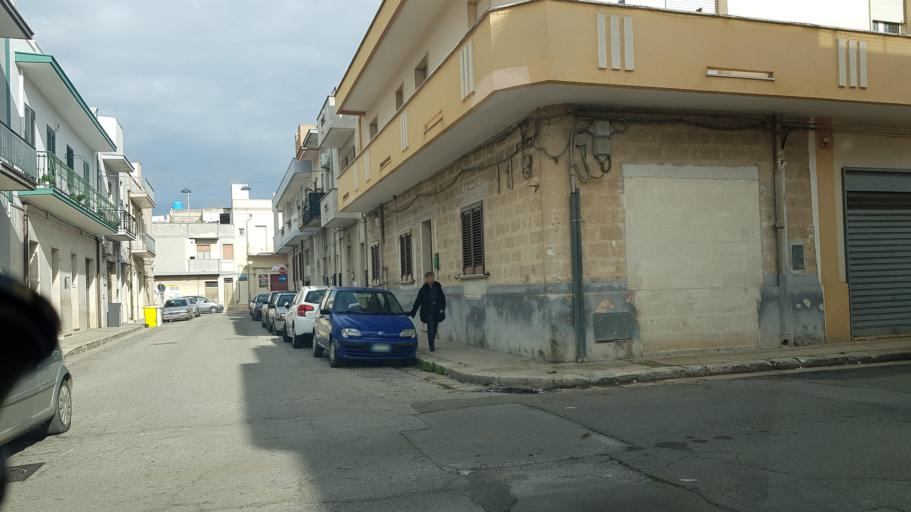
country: IT
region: Apulia
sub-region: Provincia di Brindisi
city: Francavilla Fontana
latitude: 40.5240
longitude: 17.5799
